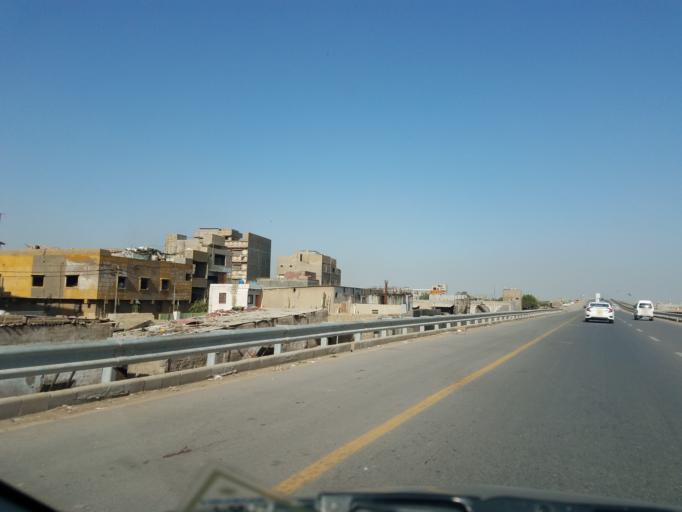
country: PK
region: Sindh
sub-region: Karachi District
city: Karachi
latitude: 24.8799
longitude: 66.9904
